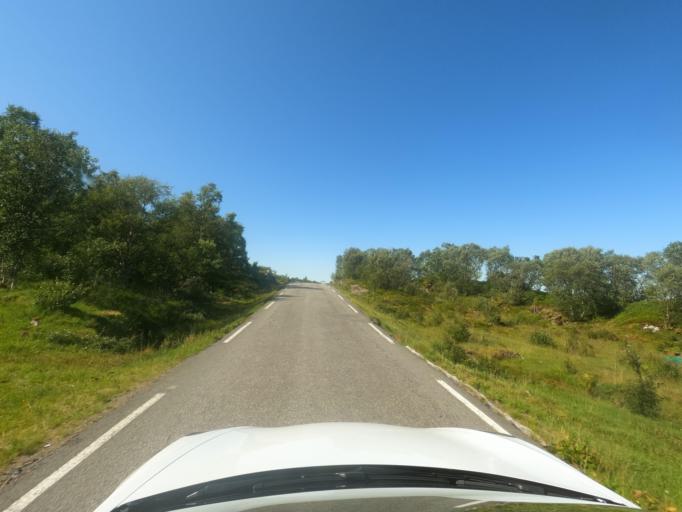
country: NO
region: Nordland
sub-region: Hadsel
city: Melbu
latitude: 68.4337
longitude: 14.7629
